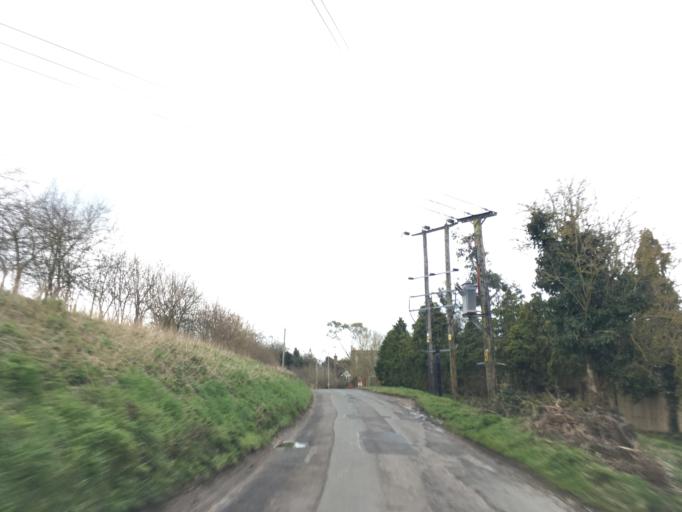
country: GB
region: England
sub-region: West Berkshire
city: Hungerford
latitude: 51.4218
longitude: -1.5102
